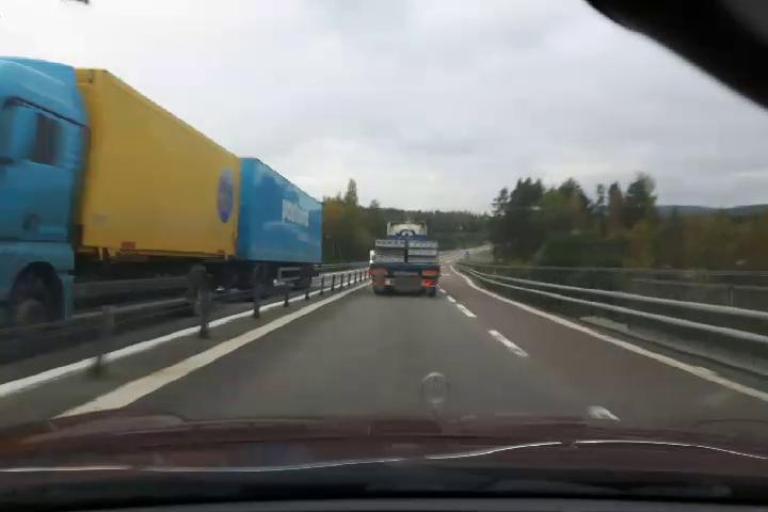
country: SE
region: Vaesternorrland
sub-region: Haernoesands Kommun
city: Haernoesand
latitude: 62.7705
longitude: 17.9146
